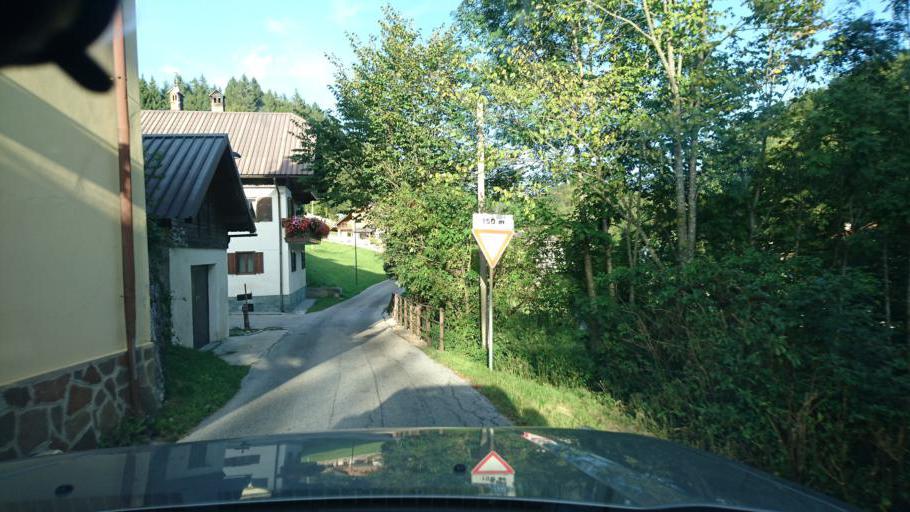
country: AT
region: Carinthia
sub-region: Politischer Bezirk Villach Land
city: Hohenthurn
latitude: 46.4963
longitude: 13.6578
